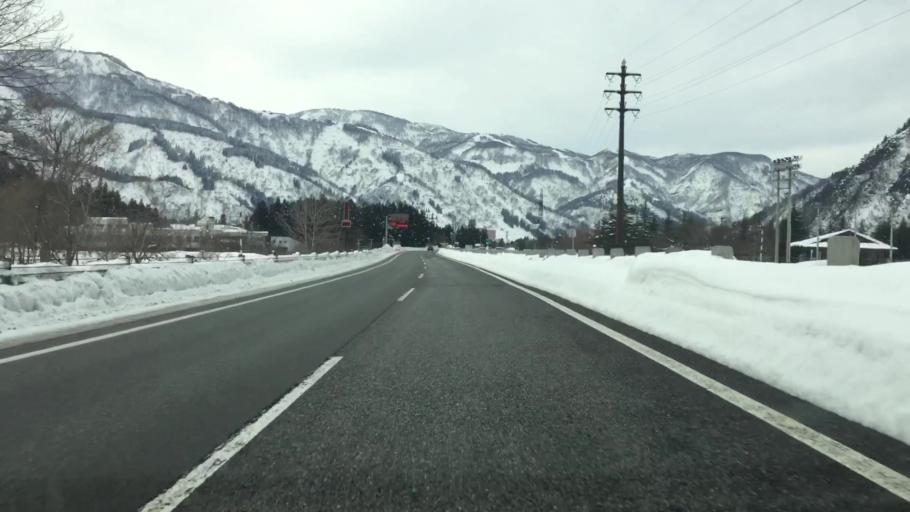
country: JP
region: Niigata
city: Shiozawa
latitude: 36.9297
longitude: 138.8357
